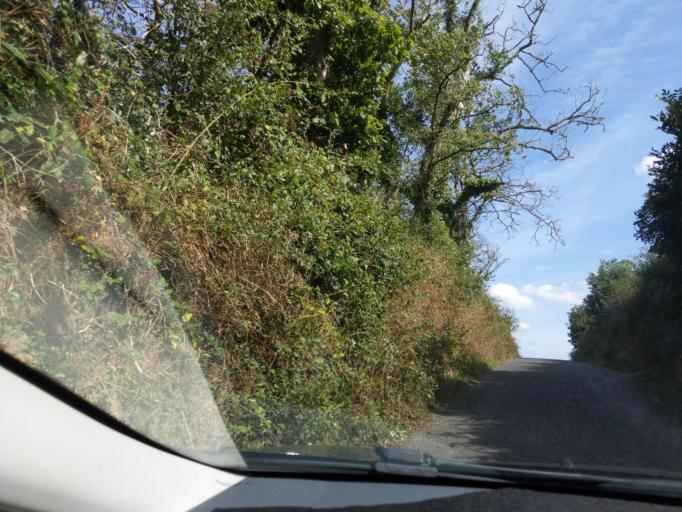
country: GB
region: England
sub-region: Cornwall
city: Torpoint
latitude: 50.3555
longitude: -4.2222
